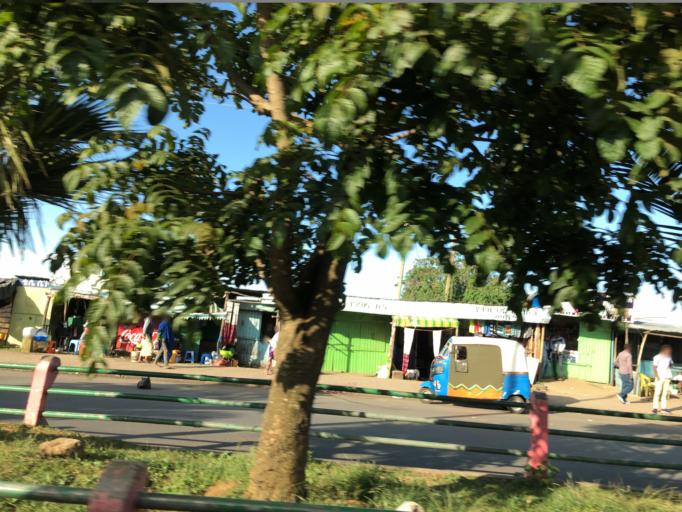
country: ET
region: Amhara
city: Debre Tabor
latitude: 11.8581
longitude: 38.0040
